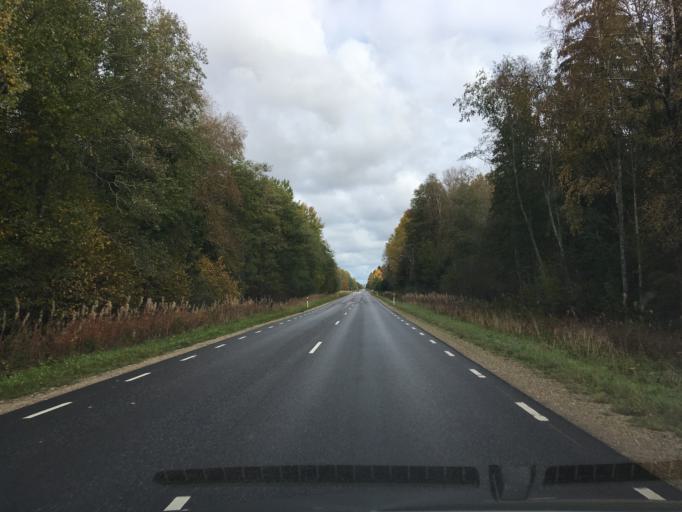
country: EE
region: Harju
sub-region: Anija vald
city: Kehra
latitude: 59.2308
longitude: 25.2805
